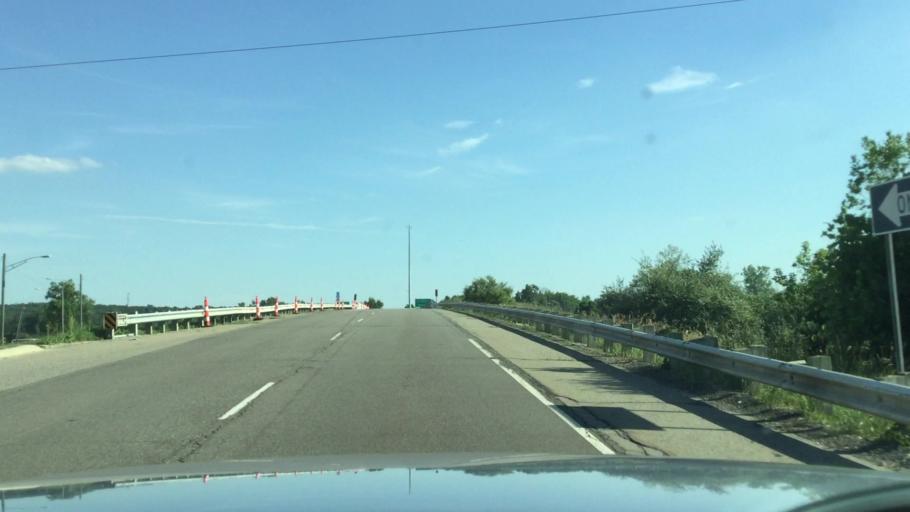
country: US
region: Michigan
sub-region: Genesee County
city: Grand Blanc
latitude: 42.8752
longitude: -83.5970
